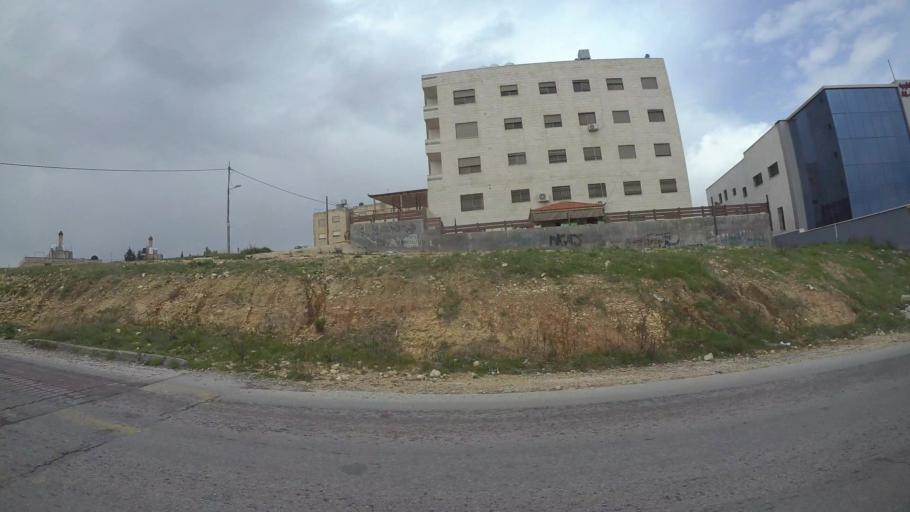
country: JO
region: Amman
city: Umm as Summaq
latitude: 31.9006
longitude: 35.8477
